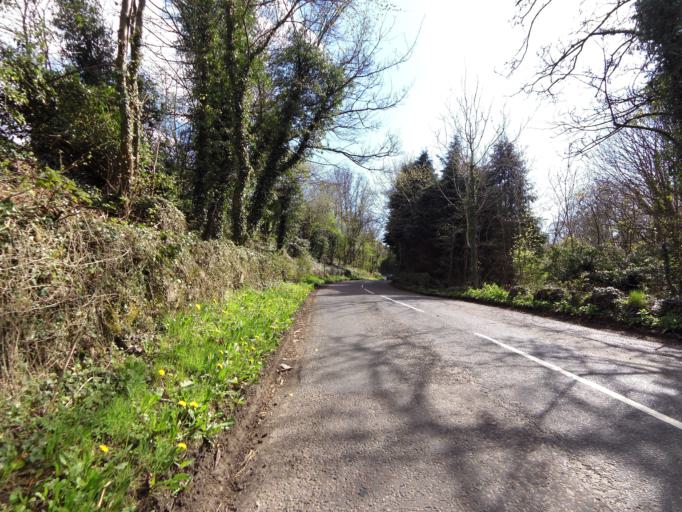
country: GB
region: Scotland
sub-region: Fife
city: Auchtermuchty
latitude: 56.3000
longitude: -3.2392
